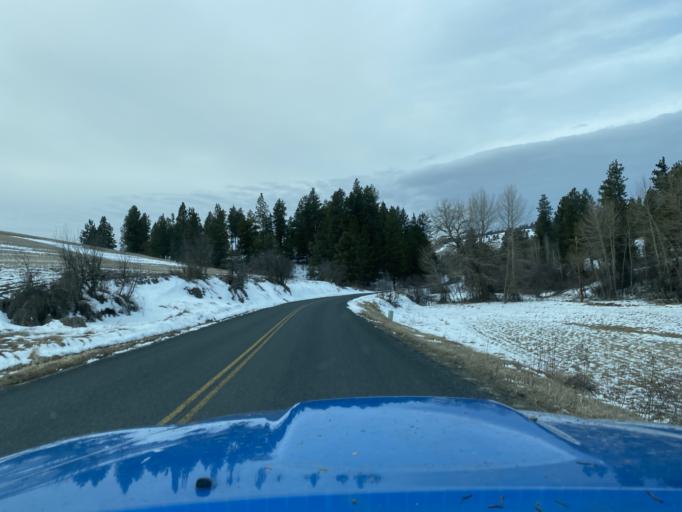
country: US
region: Idaho
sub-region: Latah County
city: Moscow
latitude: 46.6882
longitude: -116.9086
